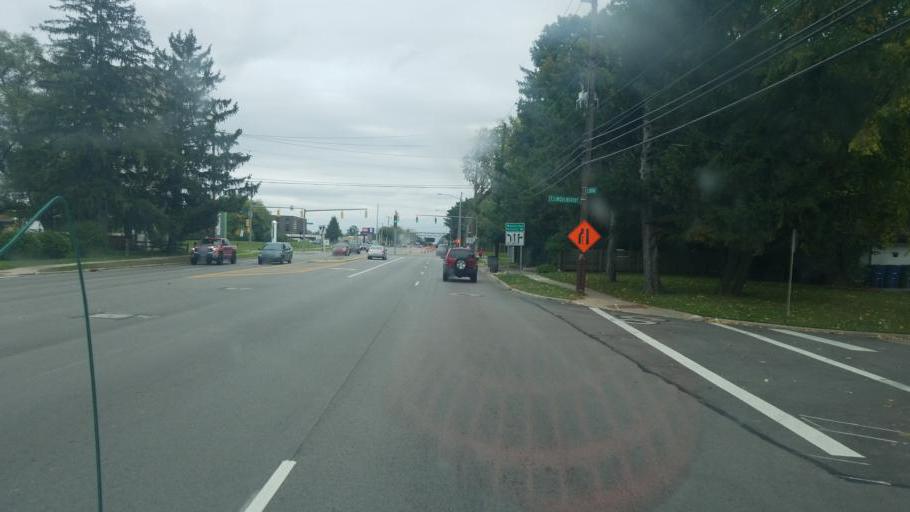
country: US
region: Ohio
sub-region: Lucas County
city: Ottawa Hills
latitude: 41.6772
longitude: -83.6308
